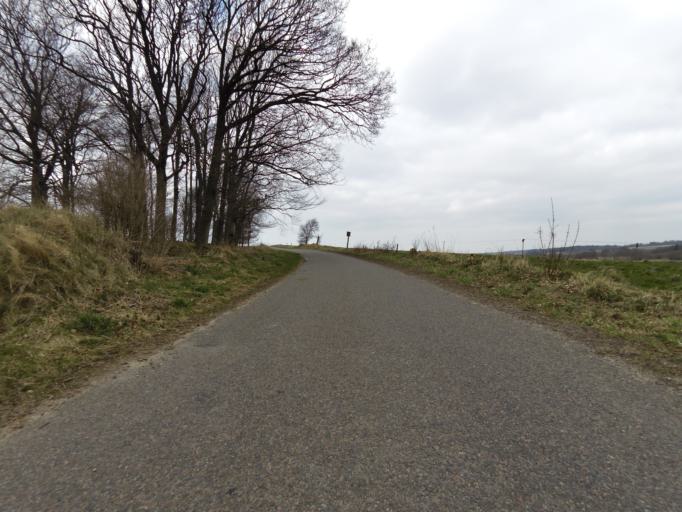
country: DK
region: Central Jutland
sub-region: Holstebro Kommune
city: Vinderup
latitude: 56.4285
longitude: 8.7331
